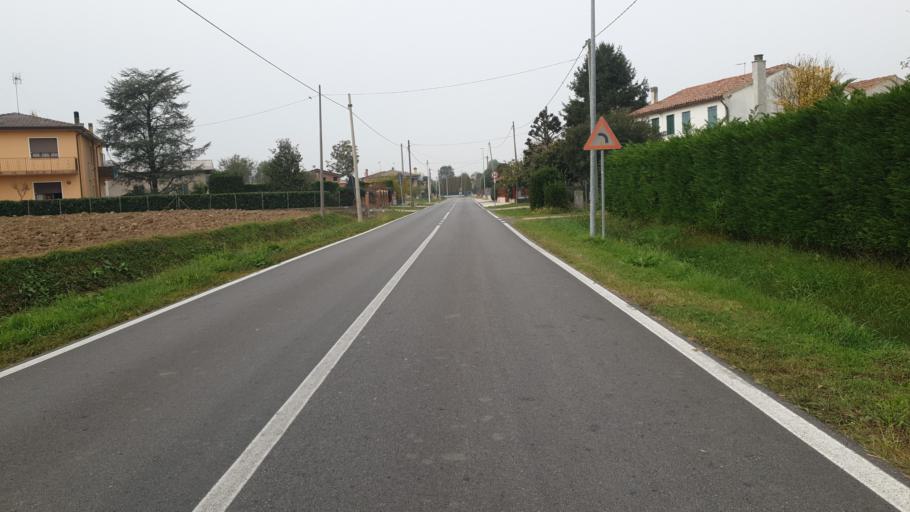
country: IT
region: Veneto
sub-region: Provincia di Padova
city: Bertipaglia
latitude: 45.3059
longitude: 11.8970
